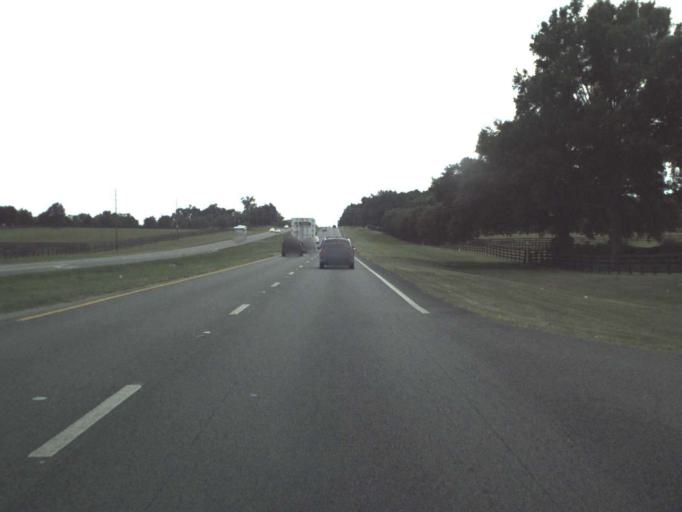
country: US
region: Florida
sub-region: Marion County
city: Citra
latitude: 29.3129
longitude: -82.1519
